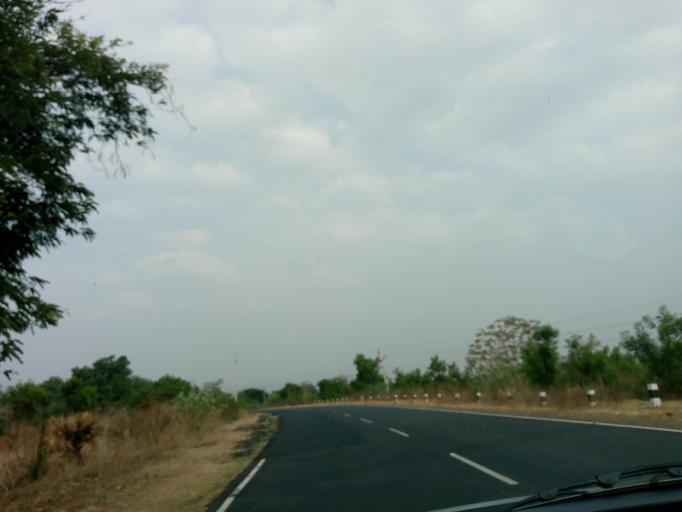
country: IN
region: Andhra Pradesh
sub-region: Prakasam
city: Diguvametta
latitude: 15.3784
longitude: 78.8681
